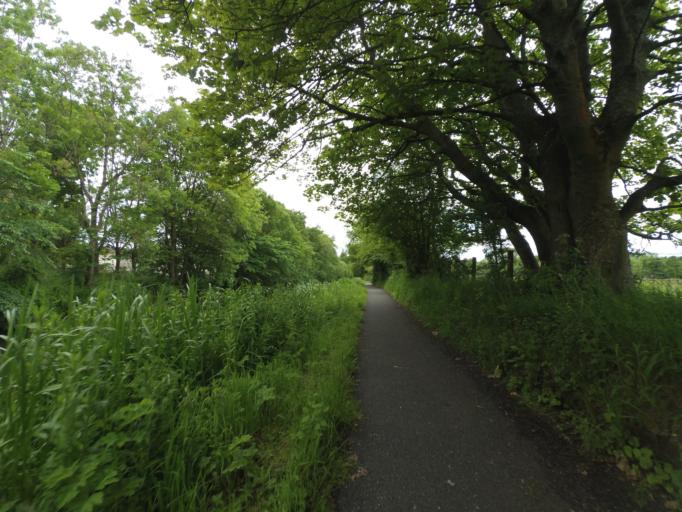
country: GB
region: Scotland
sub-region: Falkirk
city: Polmont
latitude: 55.9827
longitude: -3.7100
